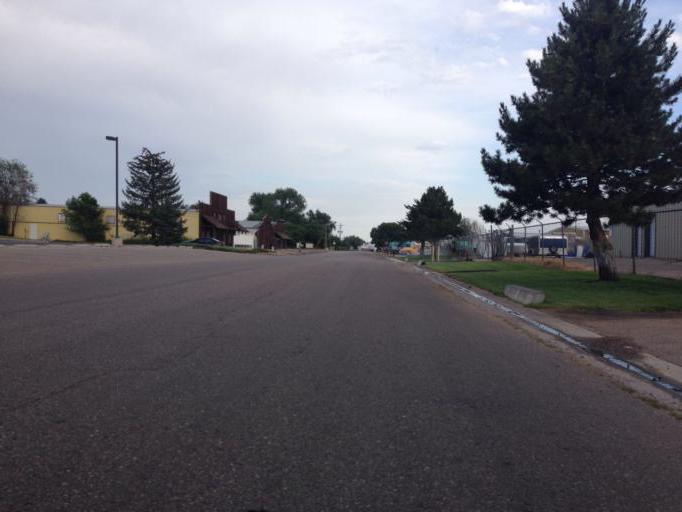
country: US
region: Colorado
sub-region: Larimer County
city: Fort Collins
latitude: 40.5853
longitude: -105.0443
